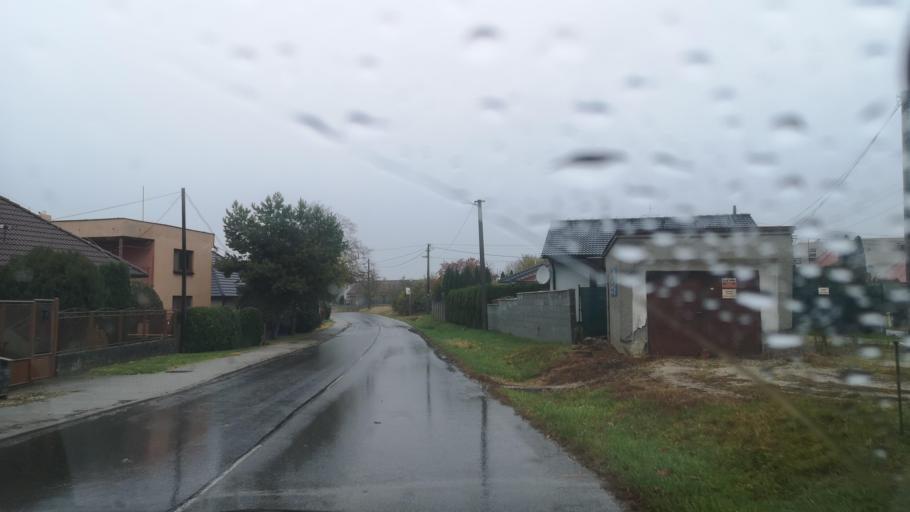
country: SK
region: Nitriansky
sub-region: Okres Nitra
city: Nitra
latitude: 48.2900
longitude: 18.1338
